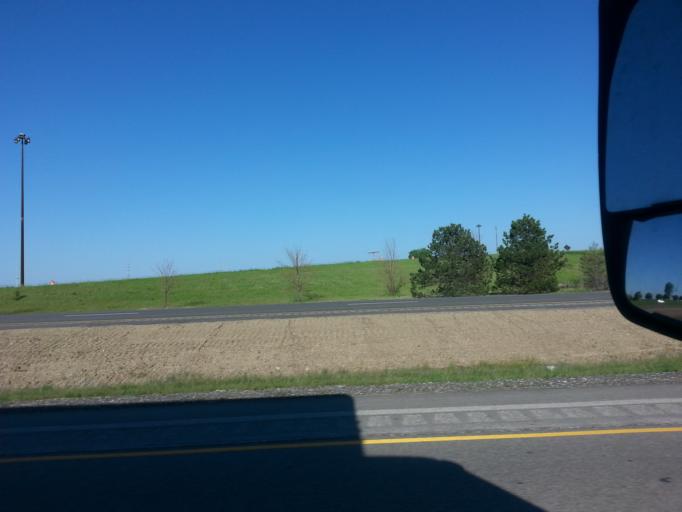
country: US
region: Illinois
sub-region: McLean County
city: Hudson
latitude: 40.5623
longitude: -89.0027
